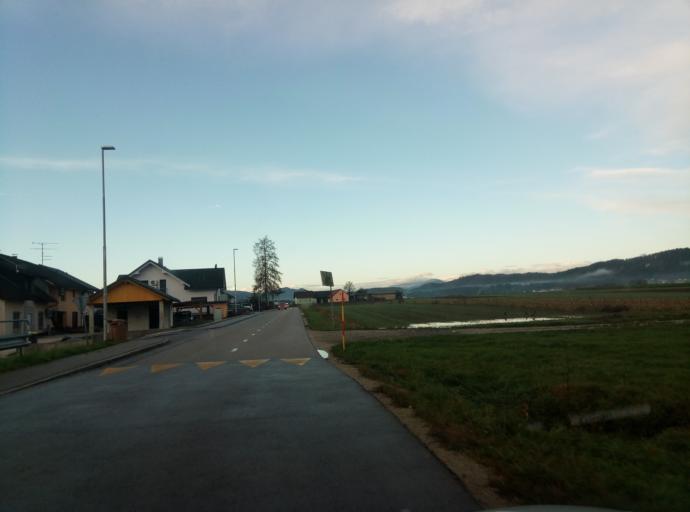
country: SI
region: Vodice
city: Vodice
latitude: 46.1604
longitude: 14.5112
